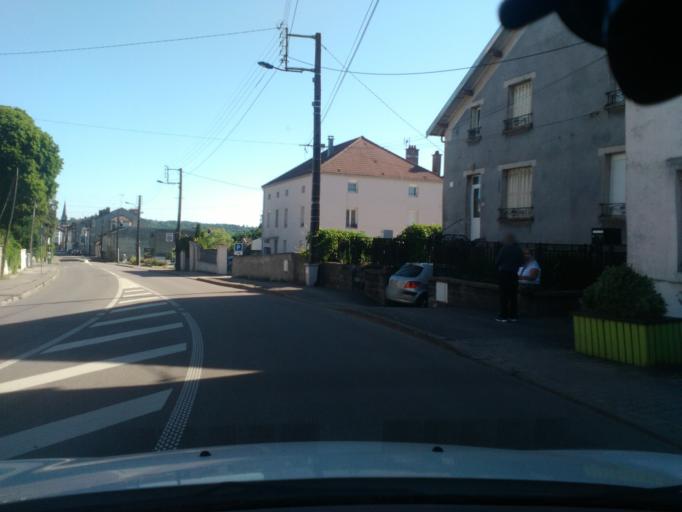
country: FR
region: Lorraine
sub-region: Departement des Vosges
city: Mirecourt
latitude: 48.2947
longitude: 6.1333
